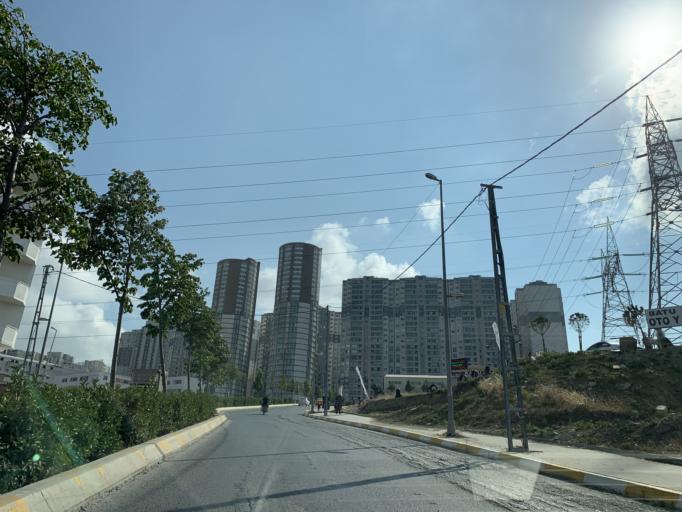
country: TR
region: Istanbul
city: Esenyurt
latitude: 41.0288
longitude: 28.6613
